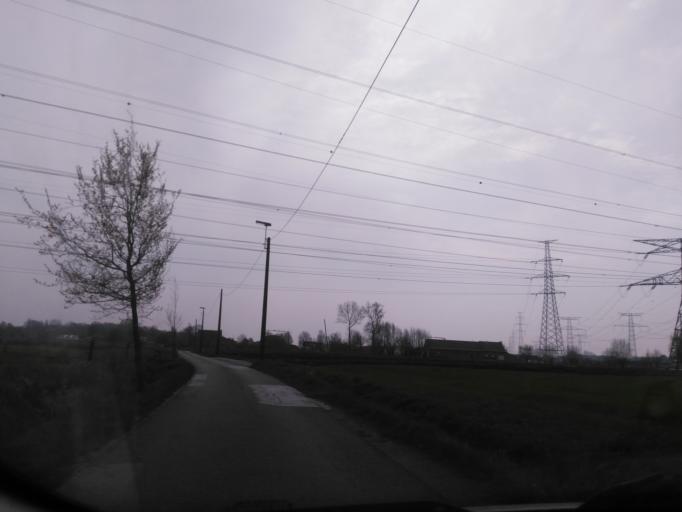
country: BE
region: Flanders
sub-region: Provincie Oost-Vlaanderen
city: Beveren
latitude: 51.2063
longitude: 4.2174
